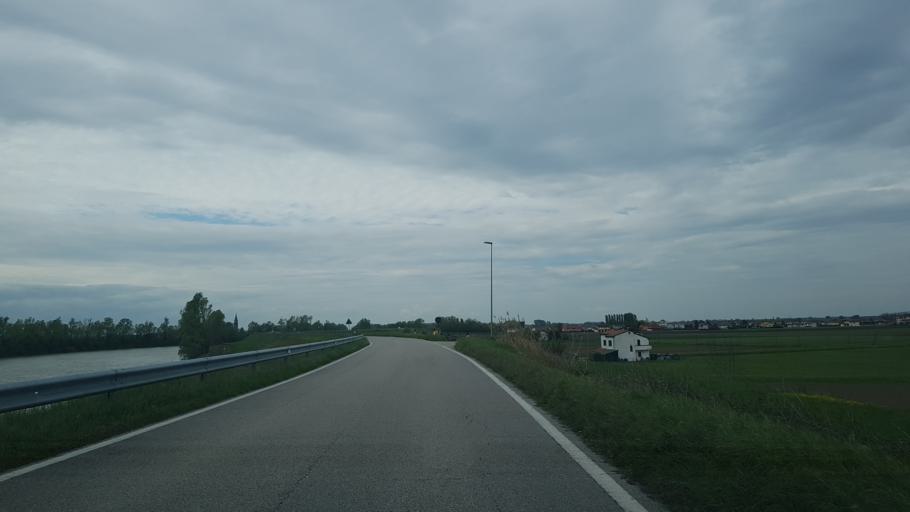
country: IT
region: Veneto
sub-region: Provincia di Padova
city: Boara Pisani
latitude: 45.0980
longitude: 11.7493
